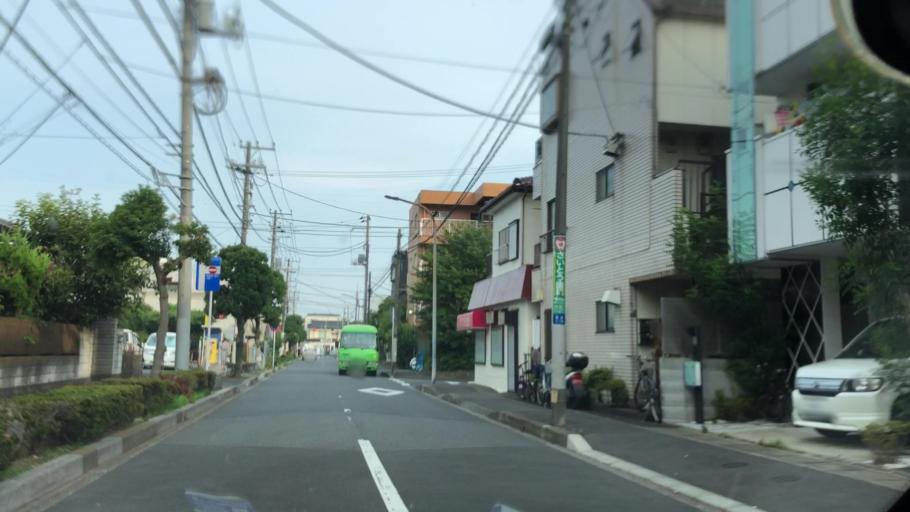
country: JP
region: Tokyo
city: Urayasu
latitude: 35.6729
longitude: 139.9094
